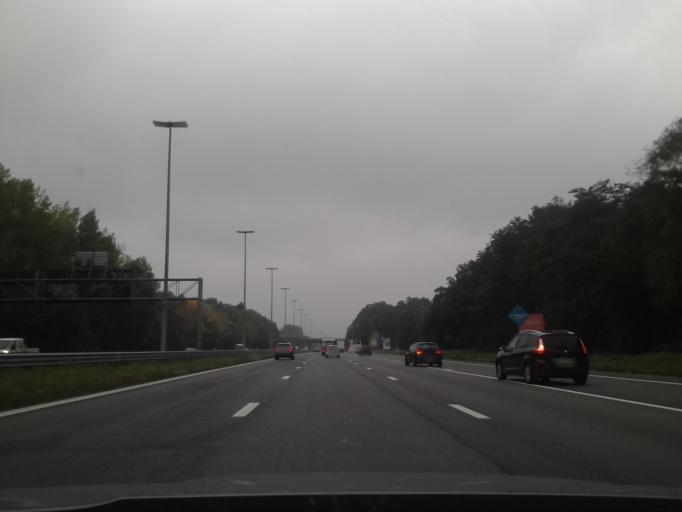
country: BE
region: Wallonia
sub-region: Province du Brabant Wallon
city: Braine-le-Chateau
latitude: 50.6580
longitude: 4.3102
